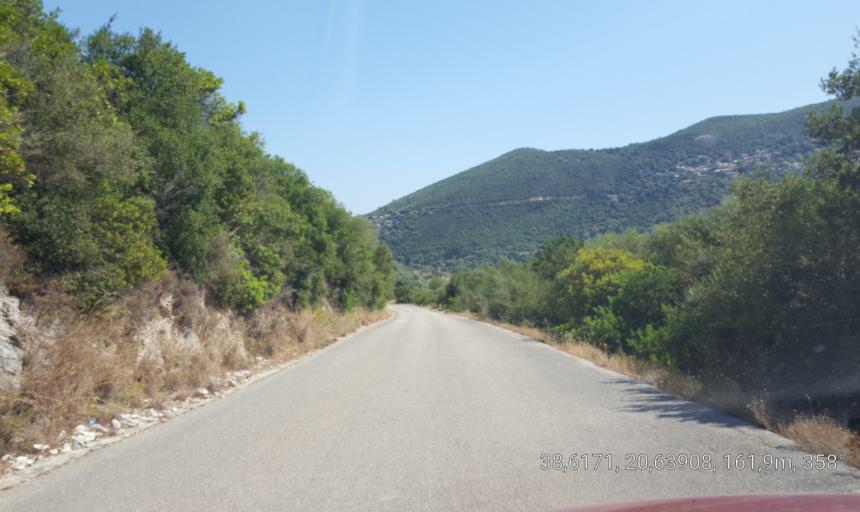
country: GR
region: Ionian Islands
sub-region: Lefkada
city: Nidri
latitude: 38.6171
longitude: 20.6391
